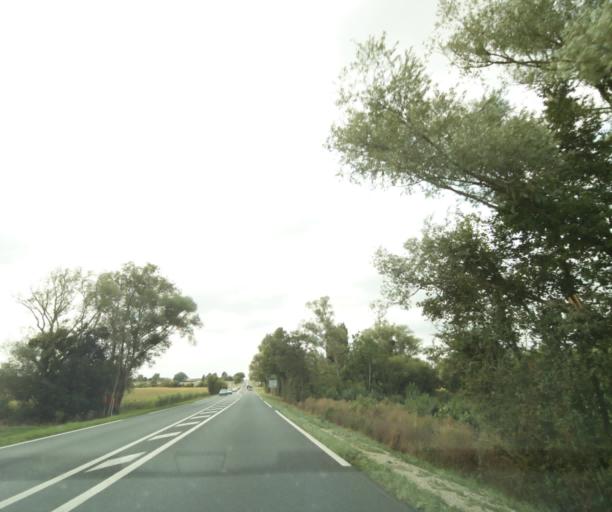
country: FR
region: Centre
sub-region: Departement de l'Indre
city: Clion
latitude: 46.9192
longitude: 1.3076
